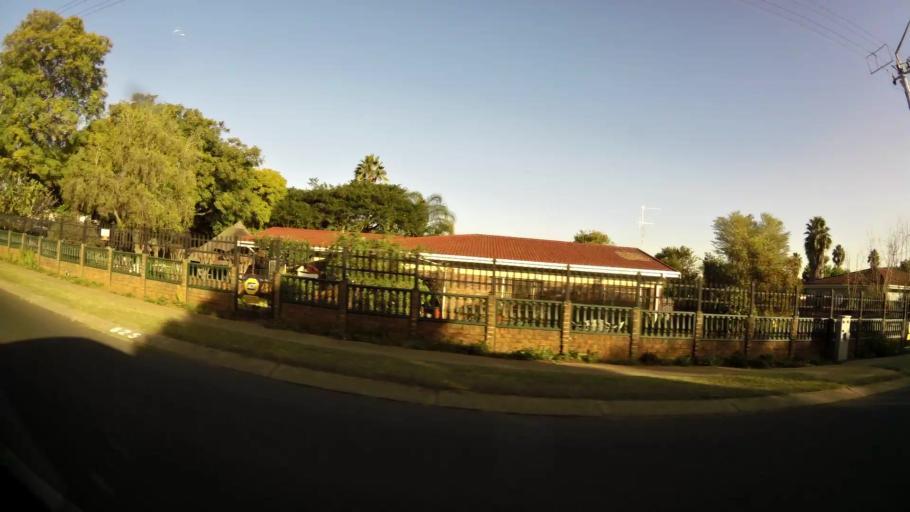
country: ZA
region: Gauteng
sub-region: City of Tshwane Metropolitan Municipality
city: Pretoria
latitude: -25.7002
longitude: 28.2201
